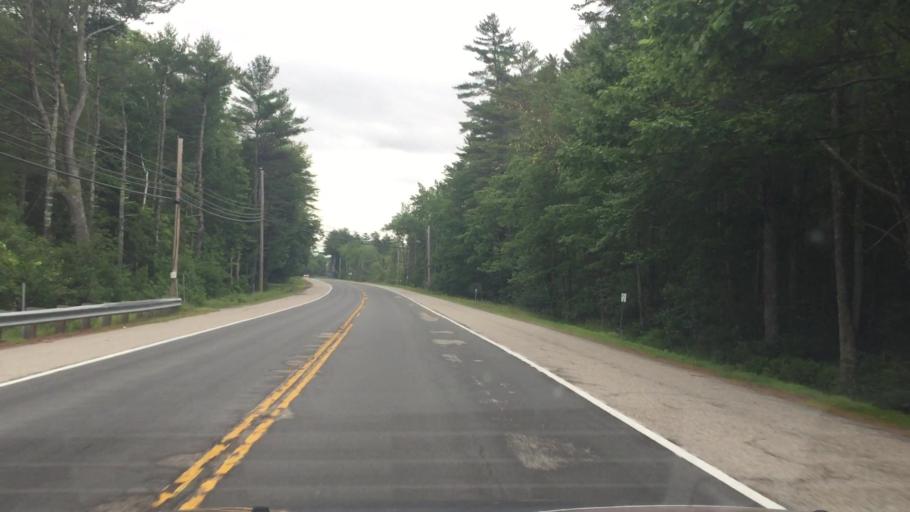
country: US
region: New Hampshire
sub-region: Carroll County
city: Tamworth
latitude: 43.8298
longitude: -71.2853
